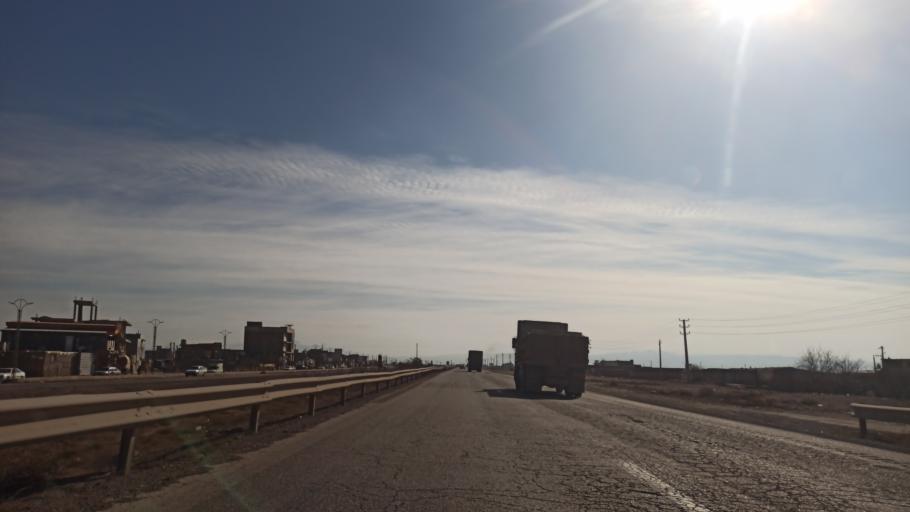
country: IR
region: Qazvin
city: Bu'in Zahra
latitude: 35.8500
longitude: 50.0608
